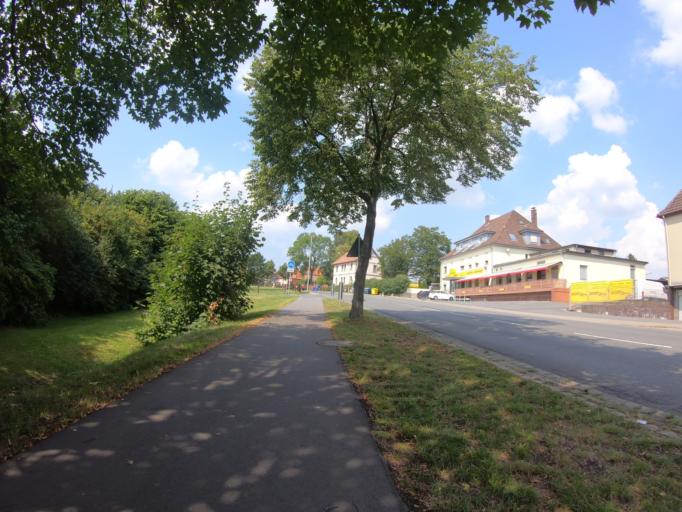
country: DE
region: Lower Saxony
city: Sickte
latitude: 52.2171
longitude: 10.6448
